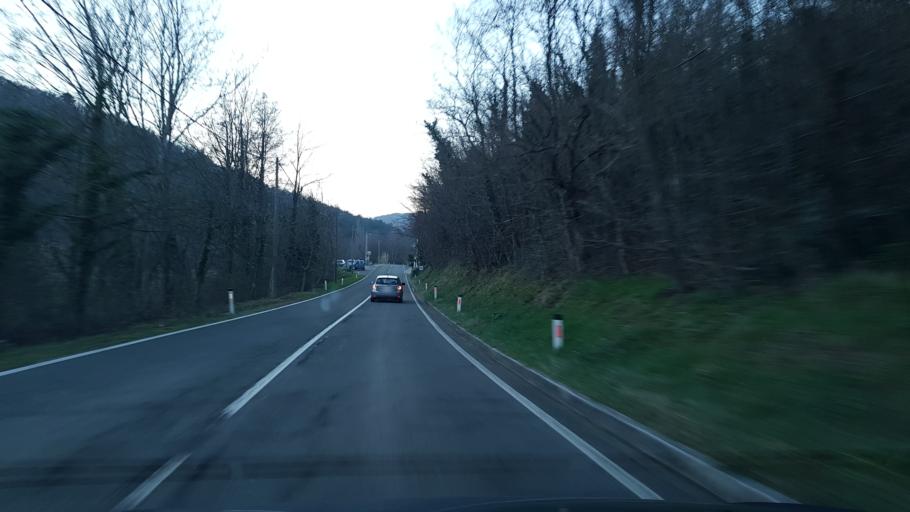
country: SI
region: Koper-Capodistria
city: Sv. Anton
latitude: 45.5369
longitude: 13.8647
